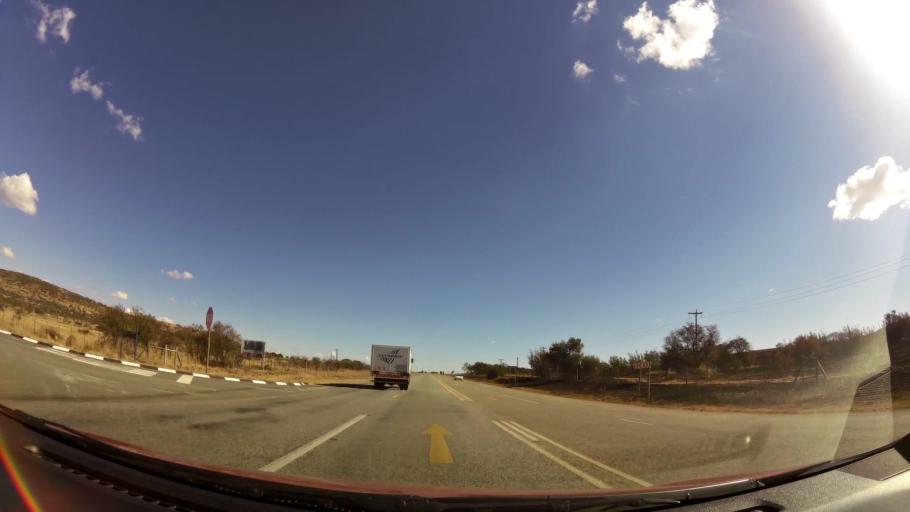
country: ZA
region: North-West
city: Fochville
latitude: -26.4391
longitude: 27.4972
